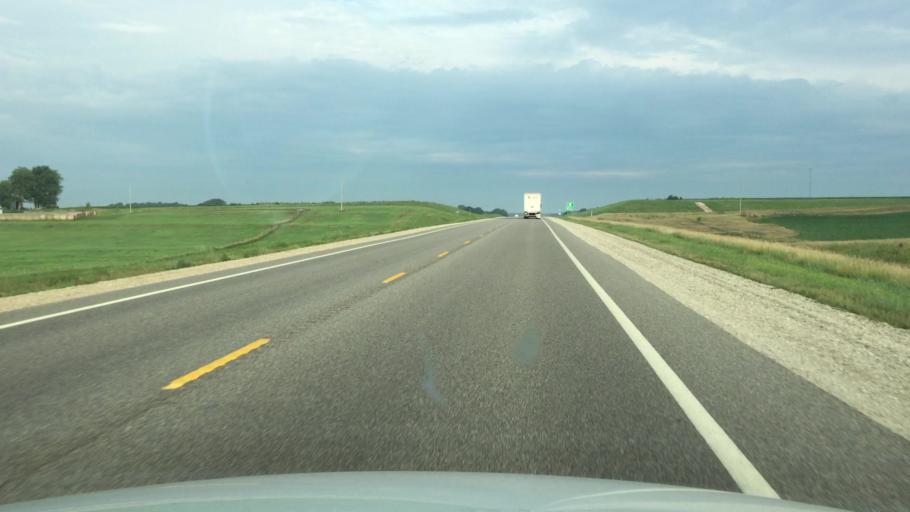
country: US
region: Kansas
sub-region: Doniphan County
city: Highland
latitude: 39.8359
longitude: -95.2426
